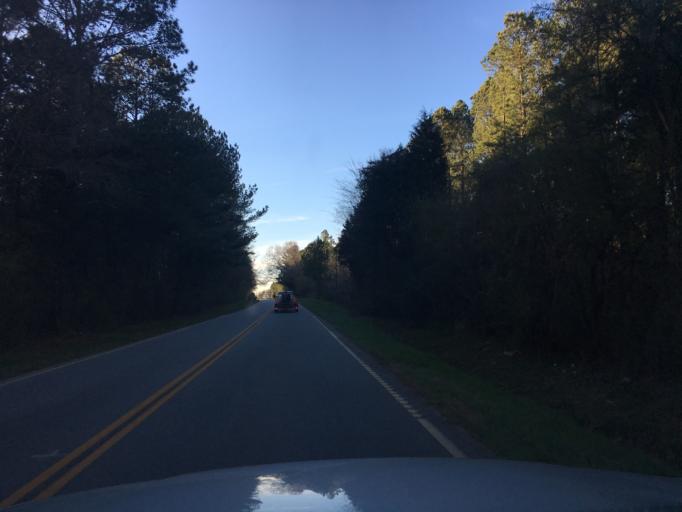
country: US
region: South Carolina
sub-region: Saluda County
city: Saluda
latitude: 34.0408
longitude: -81.8113
